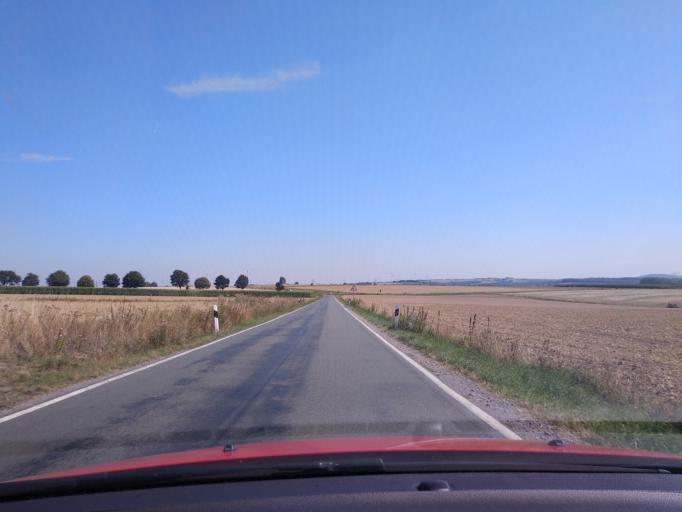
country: DE
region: North Rhine-Westphalia
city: Borgentreich
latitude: 51.6454
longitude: 9.2481
